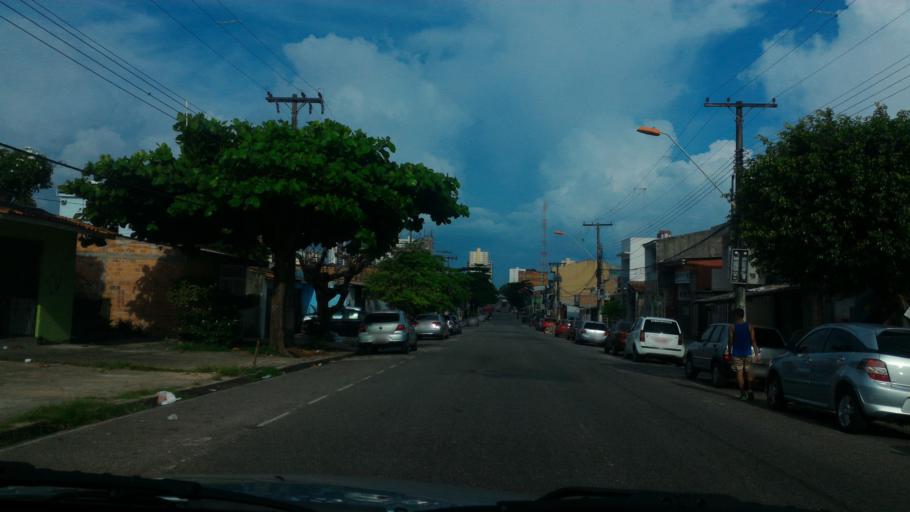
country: BR
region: Para
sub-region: Belem
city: Belem
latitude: -1.4316
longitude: -48.4695
